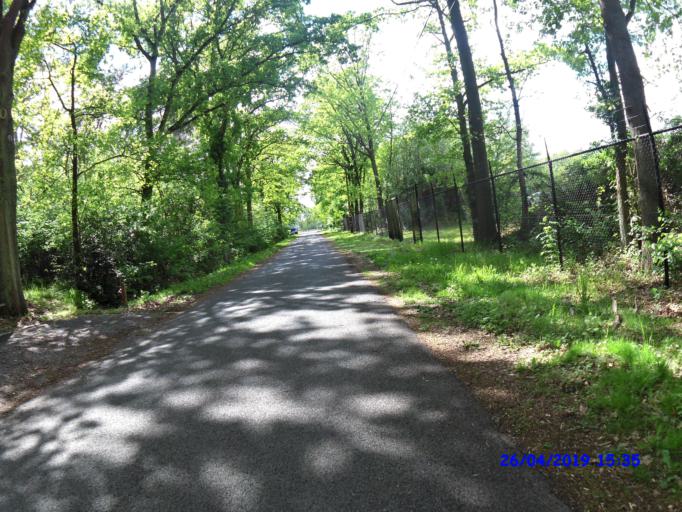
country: BE
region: Flanders
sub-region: Provincie Limburg
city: Beringen
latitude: 51.0664
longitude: 5.1975
